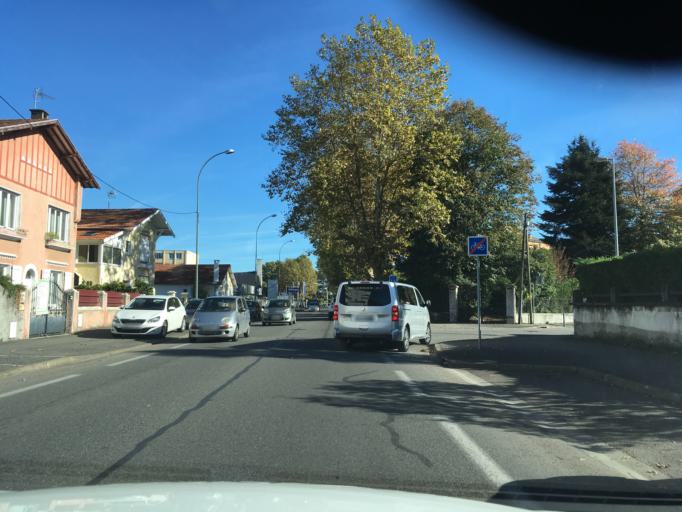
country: FR
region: Aquitaine
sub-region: Departement des Pyrenees-Atlantiques
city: Bizanos
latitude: 43.3078
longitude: -0.3382
